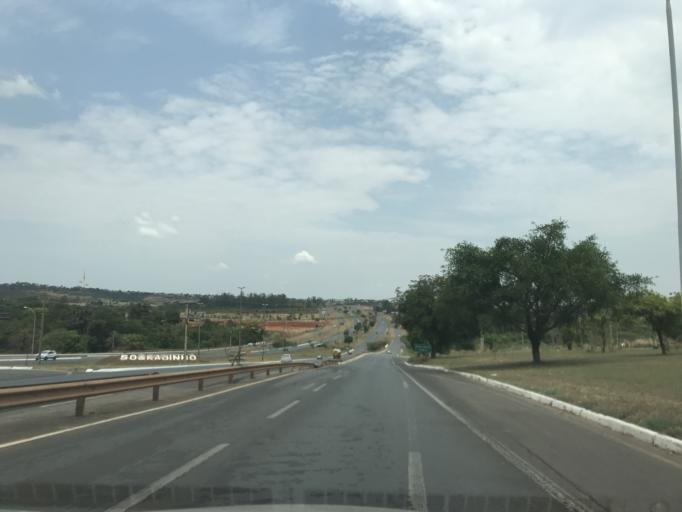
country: BR
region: Federal District
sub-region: Brasilia
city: Brasilia
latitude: -15.6644
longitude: -47.8061
